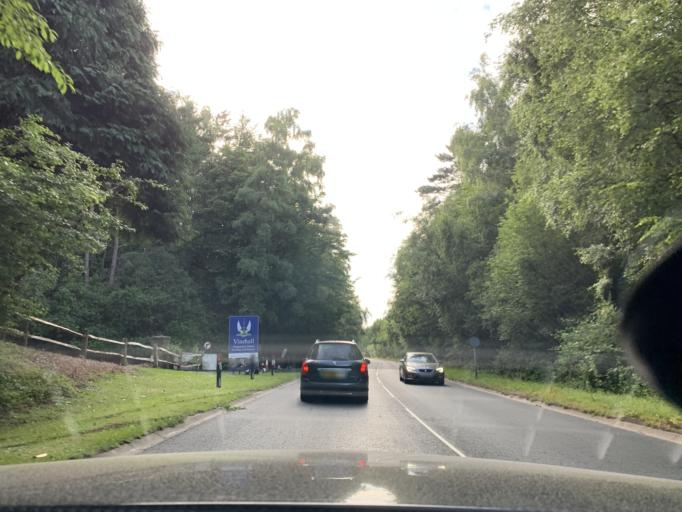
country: GB
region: England
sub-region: East Sussex
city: Robertsbridge
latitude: 50.9591
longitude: 0.4912
